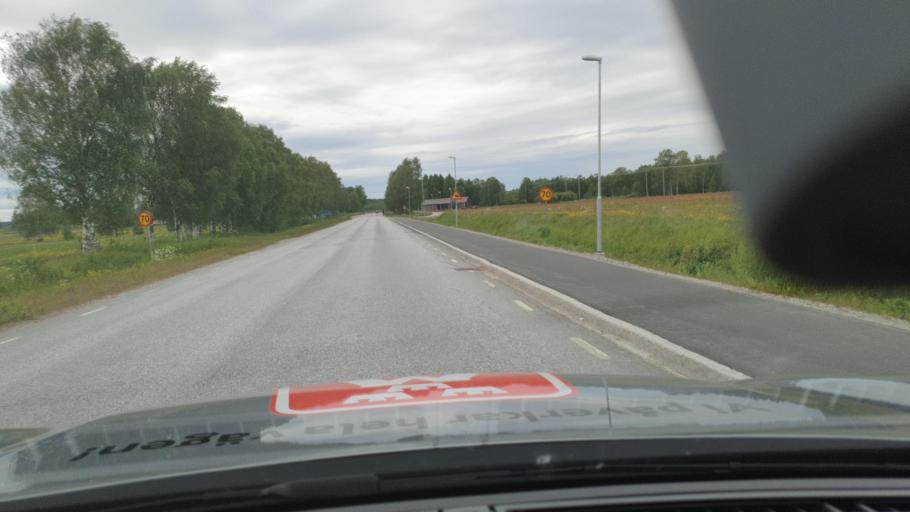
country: SE
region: Norrbotten
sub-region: Kalix Kommun
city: Rolfs
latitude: 65.8801
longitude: 23.0810
